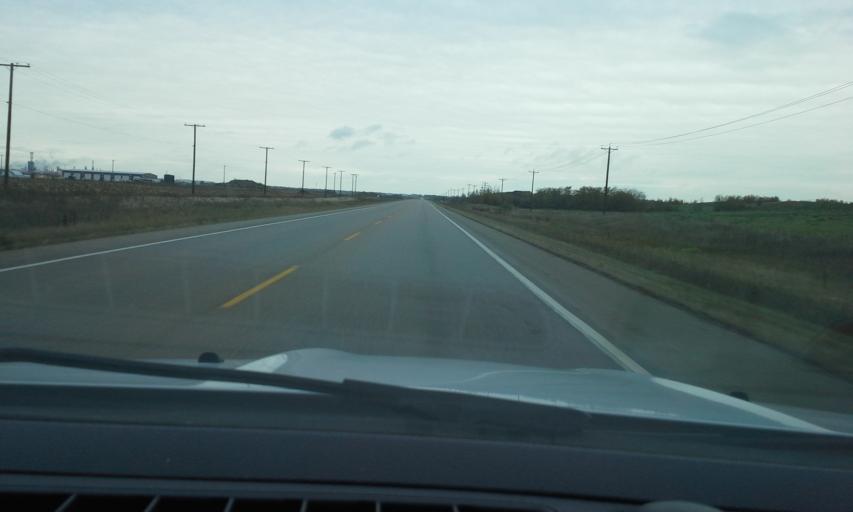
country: CA
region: Saskatchewan
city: Lloydminster
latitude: 53.2780
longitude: -109.8872
